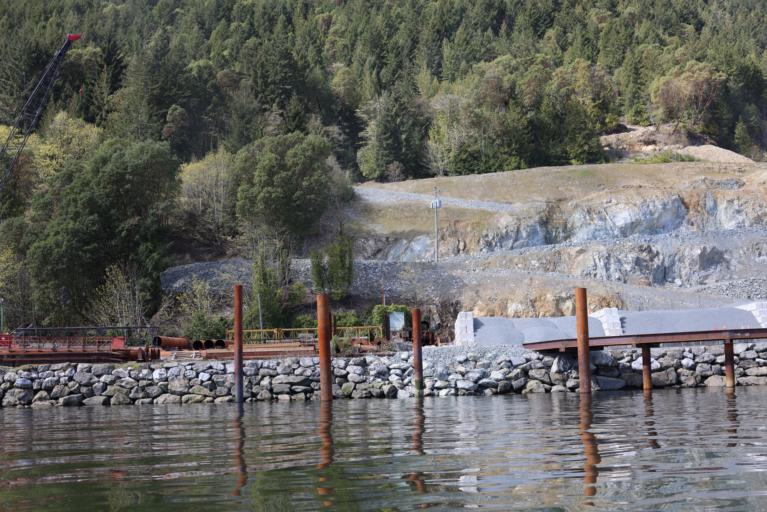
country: CA
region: British Columbia
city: North Saanich
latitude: 48.5844
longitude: -123.5201
